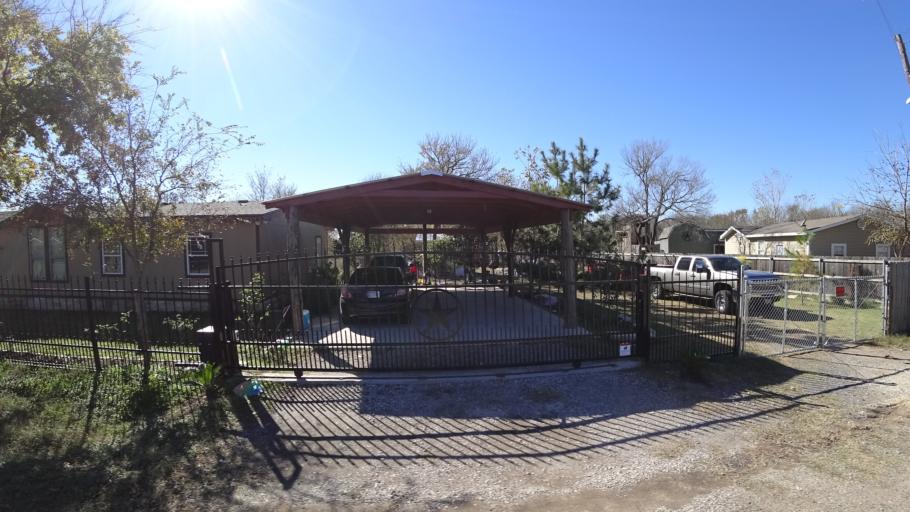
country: US
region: Texas
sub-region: Travis County
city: Garfield
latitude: 30.1275
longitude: -97.6150
